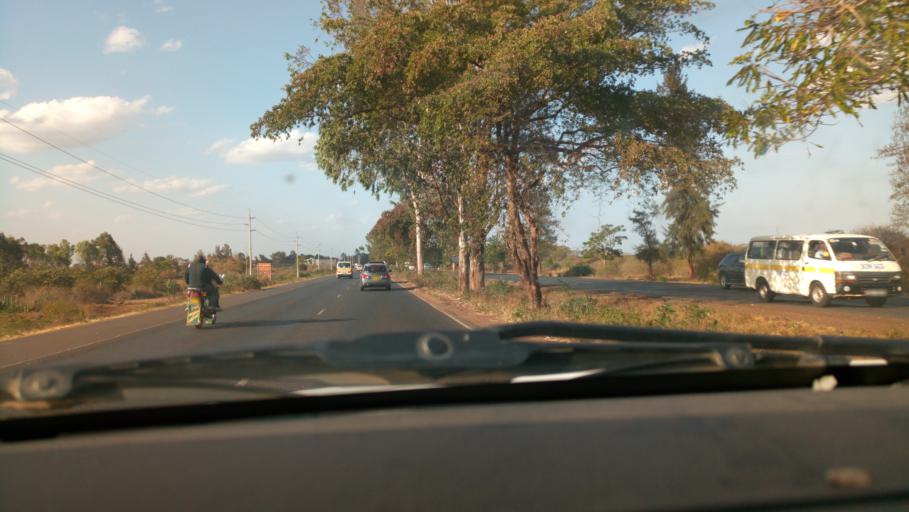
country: KE
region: Nairobi Area
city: Thika
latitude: -1.0160
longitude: 37.0727
